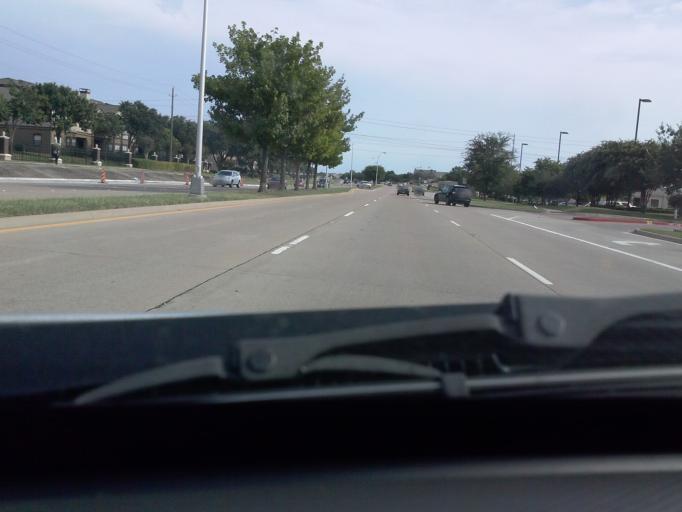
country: US
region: Texas
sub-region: Collin County
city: Frisco
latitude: 33.0640
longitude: -96.7963
